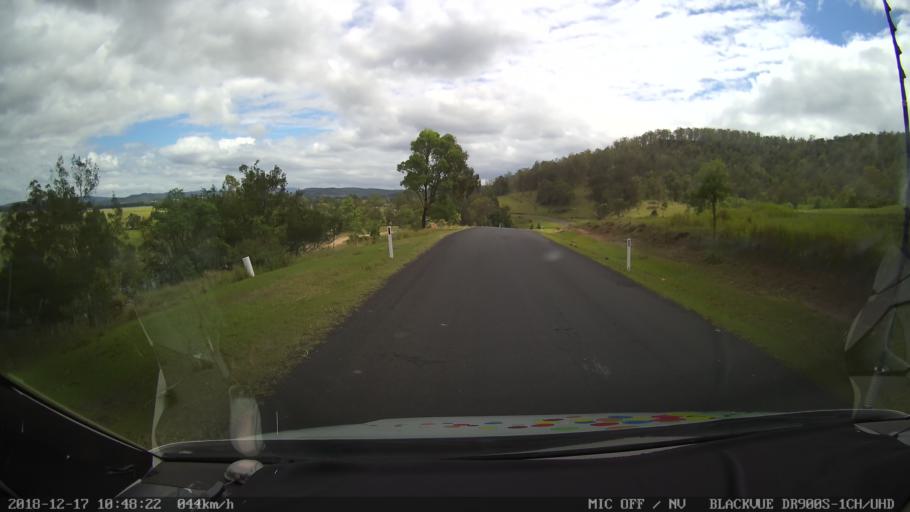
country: AU
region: New South Wales
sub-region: Clarence Valley
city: Gordon
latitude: -28.8736
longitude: 152.5708
